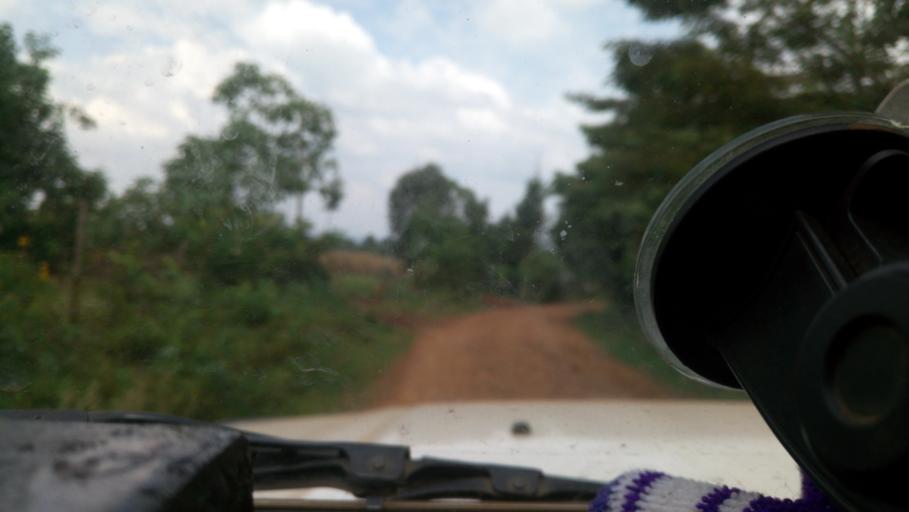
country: KE
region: Kericho
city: Sotik
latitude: -0.6259
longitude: 35.1029
